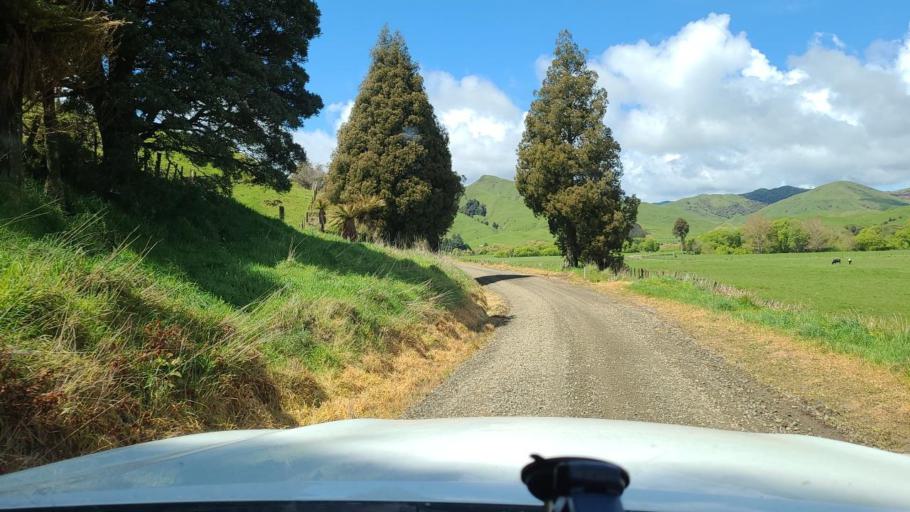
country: NZ
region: Bay of Plenty
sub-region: Opotiki District
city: Opotiki
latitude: -38.2531
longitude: 177.5584
